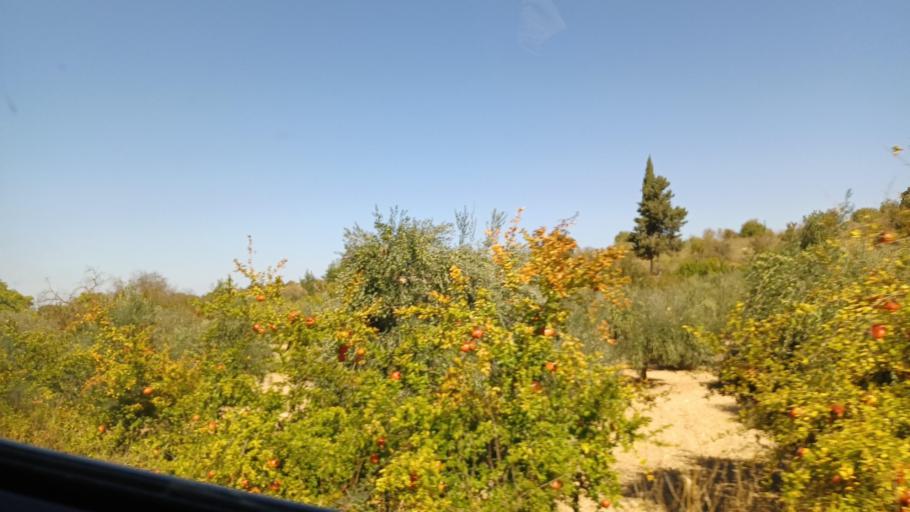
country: CY
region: Pafos
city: Mesogi
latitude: 34.9290
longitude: 32.5494
